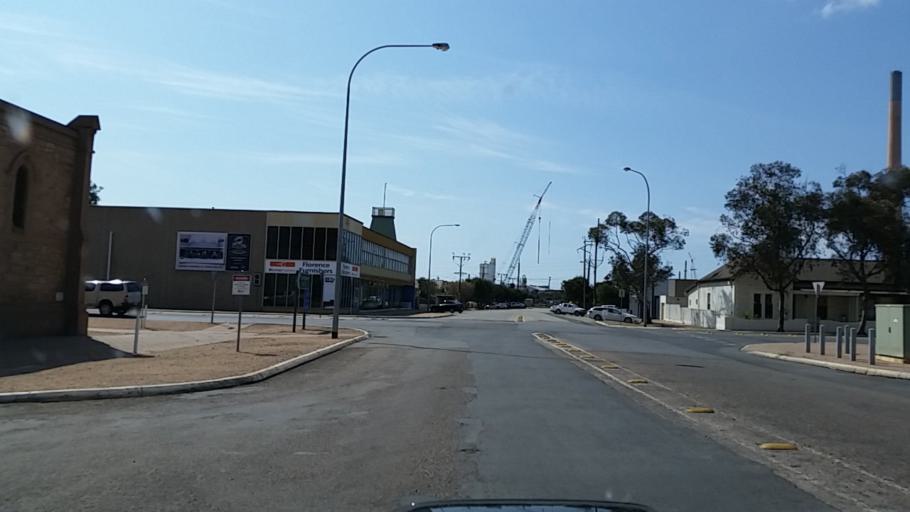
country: AU
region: South Australia
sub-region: Port Pirie City and Dists
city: Port Pirie
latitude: -33.1758
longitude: 138.0084
